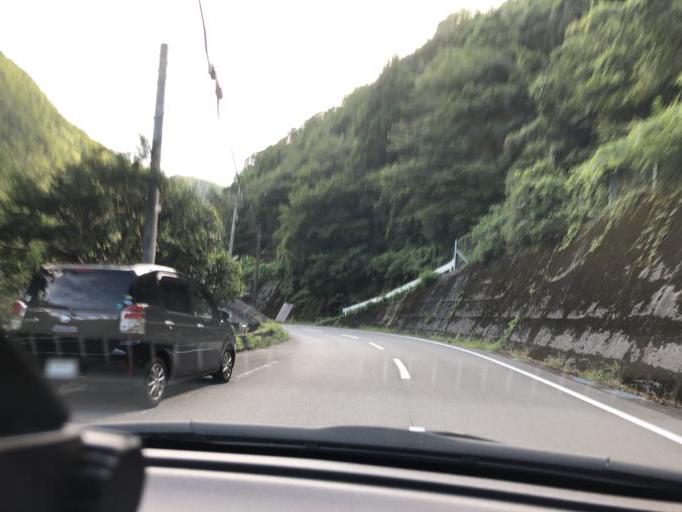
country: JP
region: Kochi
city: Kochi-shi
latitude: 33.6346
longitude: 133.5199
